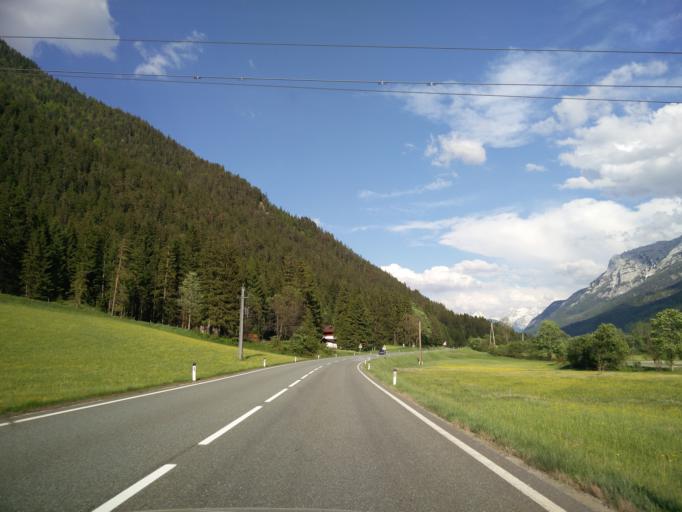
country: AT
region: Tyrol
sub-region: Politischer Bezirk Kitzbuhel
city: Waidring
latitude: 47.5885
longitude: 12.5648
